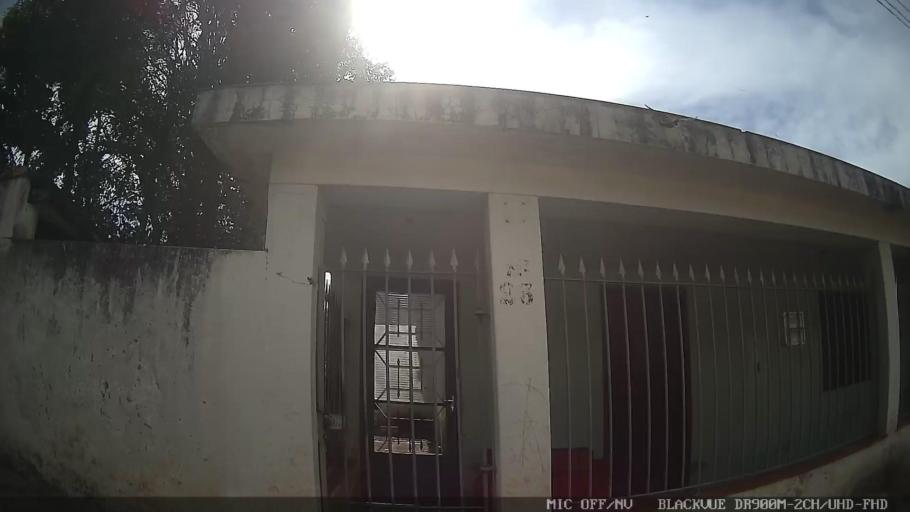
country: BR
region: Sao Paulo
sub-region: Conchas
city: Conchas
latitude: -23.0689
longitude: -47.9773
